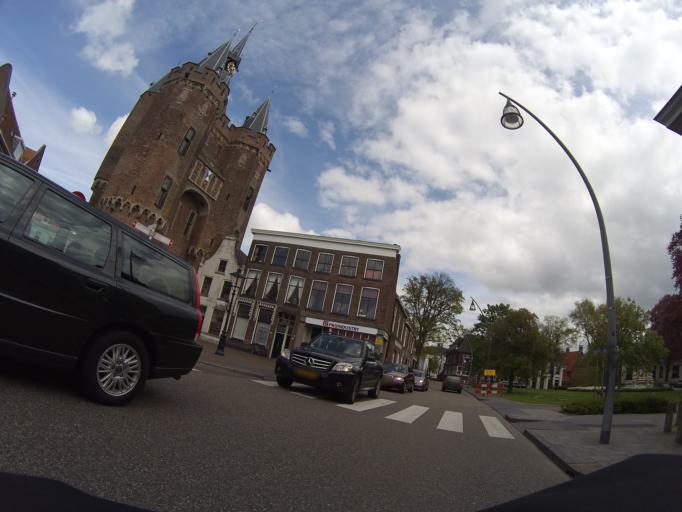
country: NL
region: Overijssel
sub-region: Gemeente Zwolle
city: Zwolle
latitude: 52.5096
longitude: 6.0955
